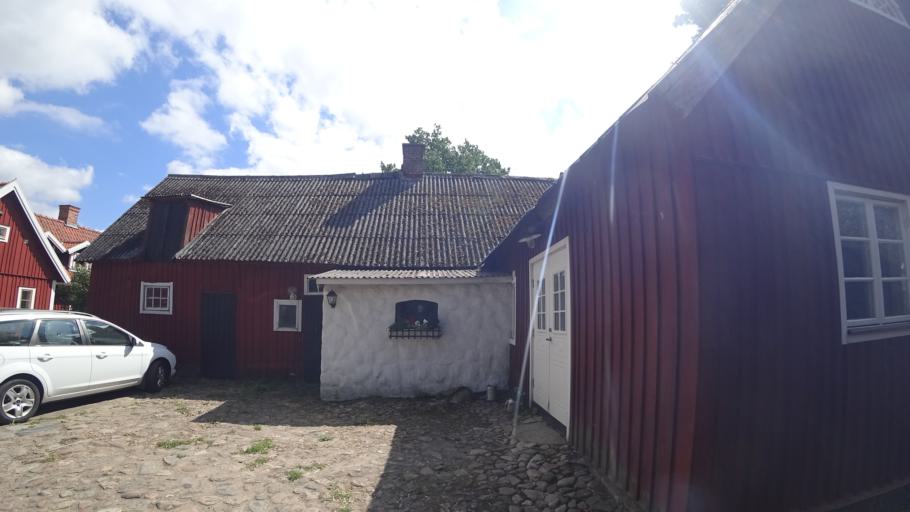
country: SE
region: Skane
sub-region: Kristianstads Kommun
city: Ahus
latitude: 55.9832
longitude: 14.2667
